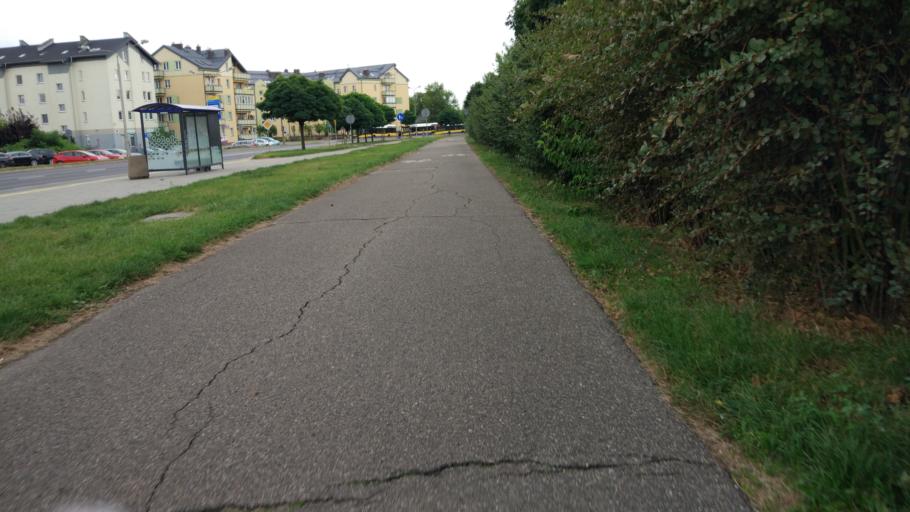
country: PL
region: Masovian Voivodeship
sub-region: Plock
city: Plock
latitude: 52.5319
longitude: 19.7587
